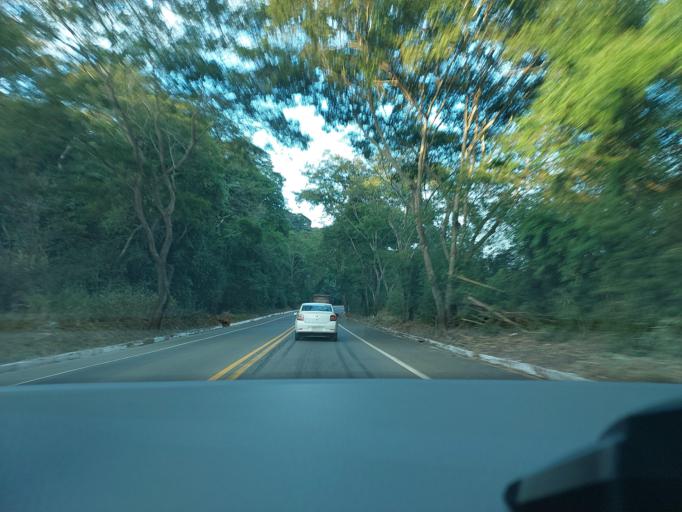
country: BR
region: Minas Gerais
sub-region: Muriae
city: Muriae
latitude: -21.1224
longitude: -42.2238
